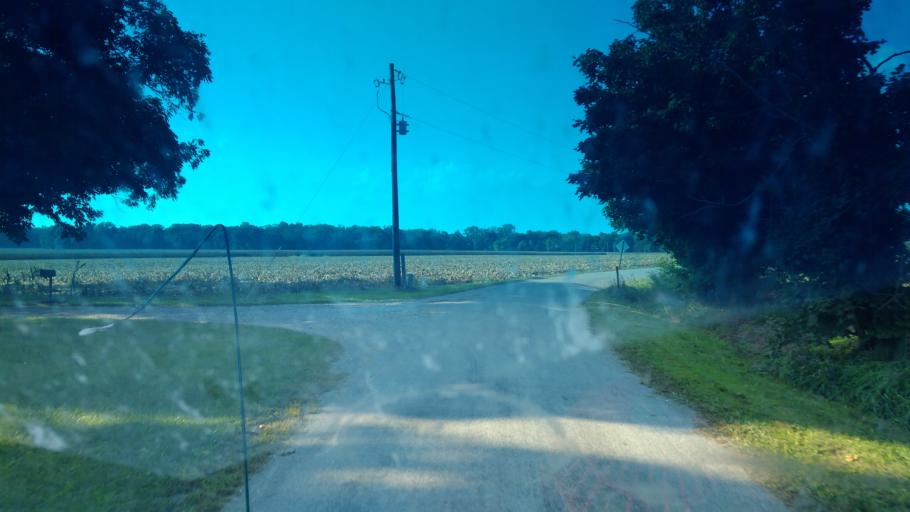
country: US
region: Ohio
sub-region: Wyandot County
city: Upper Sandusky
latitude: 40.9041
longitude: -83.2445
